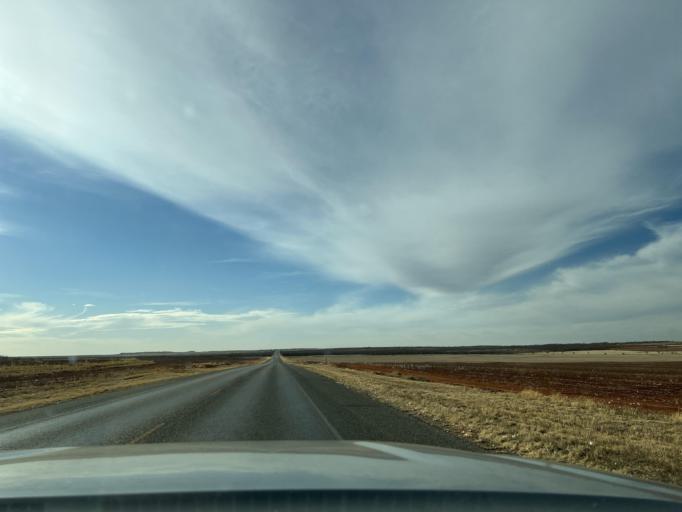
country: US
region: Texas
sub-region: Fisher County
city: Rotan
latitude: 32.7404
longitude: -100.4979
